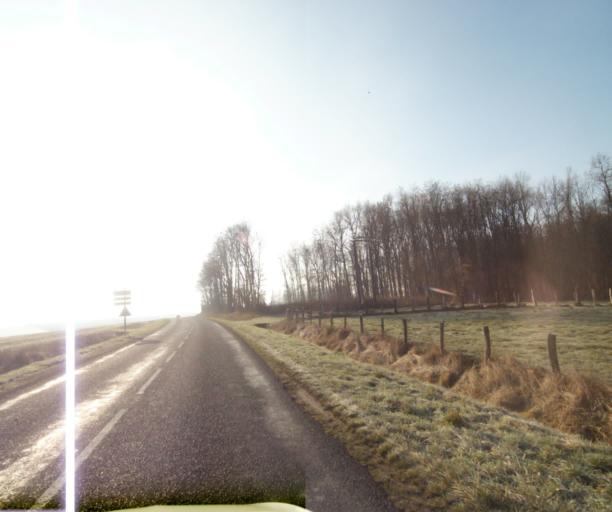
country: FR
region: Champagne-Ardenne
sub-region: Departement de la Haute-Marne
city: Montier-en-Der
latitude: 48.5068
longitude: 4.7483
